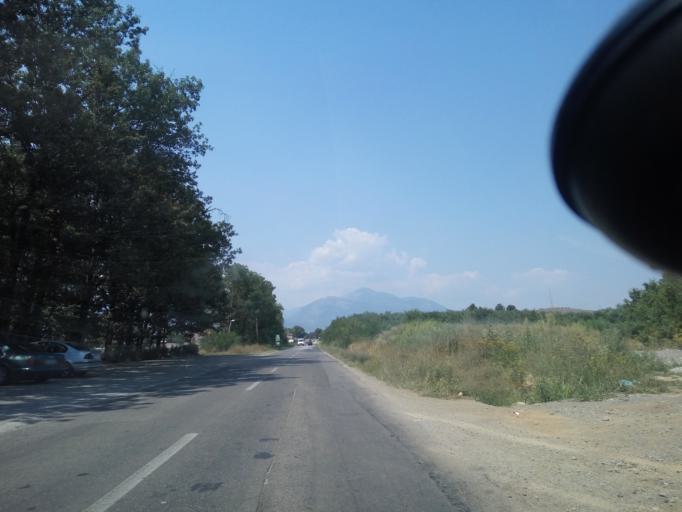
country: XK
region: Gjakova
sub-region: Komuna e Decanit
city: Gllogjan
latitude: 42.4570
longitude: 20.3547
